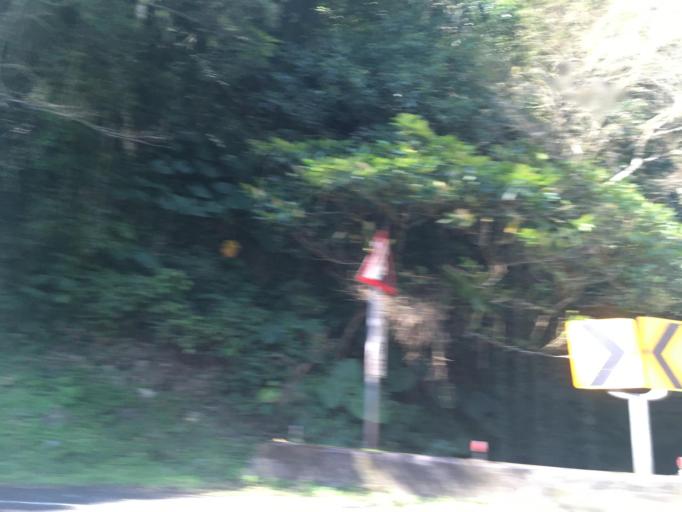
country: TW
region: Taiwan
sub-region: Yilan
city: Yilan
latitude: 24.7580
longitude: 121.6135
